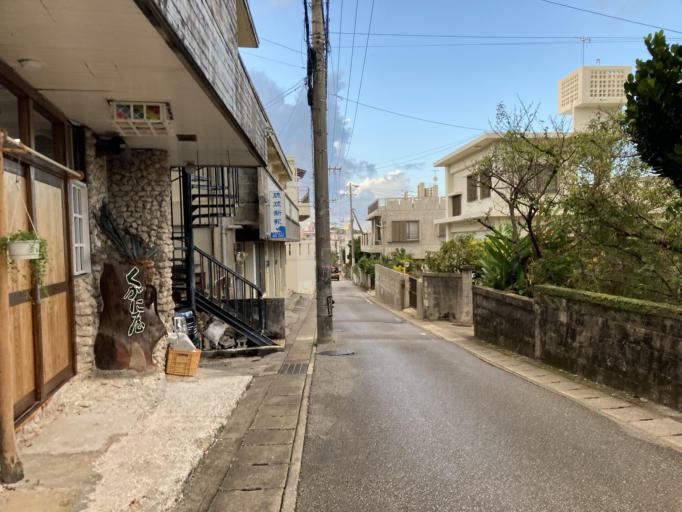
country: JP
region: Okinawa
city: Naha-shi
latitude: 26.2246
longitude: 127.7223
